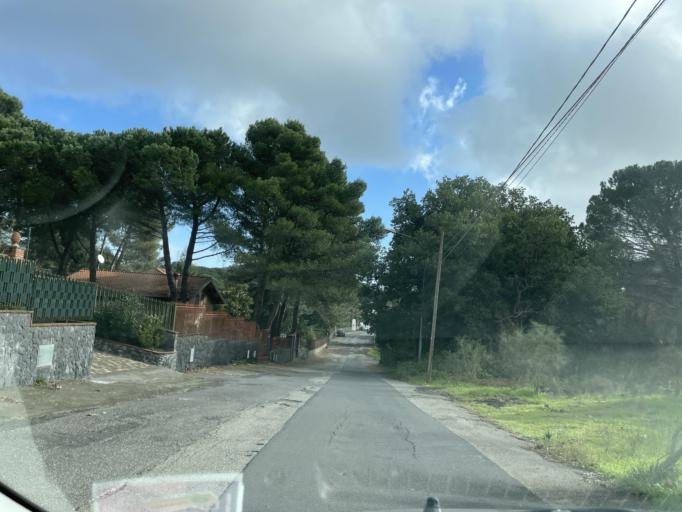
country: IT
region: Sicily
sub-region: Catania
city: Nicolosi
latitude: 37.6292
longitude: 15.0198
